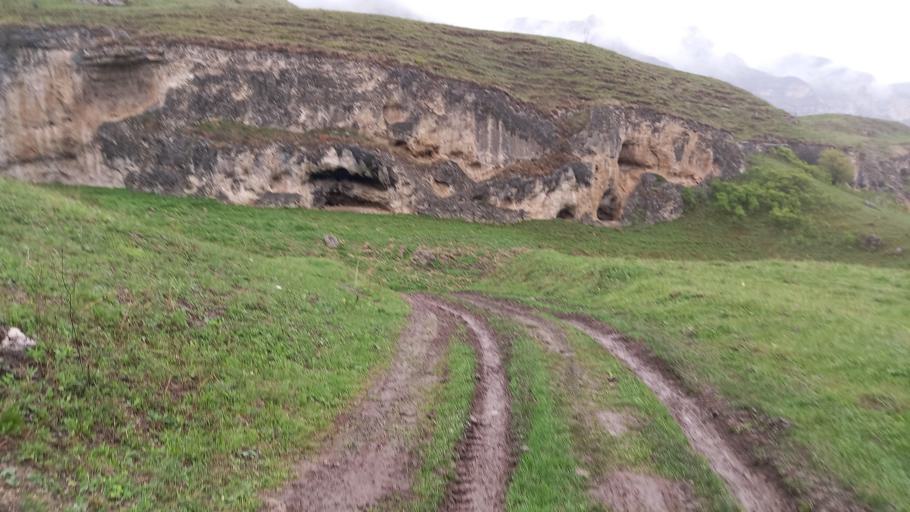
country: RU
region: Kabardino-Balkariya
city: Bylym
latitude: 43.5916
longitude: 43.0252
